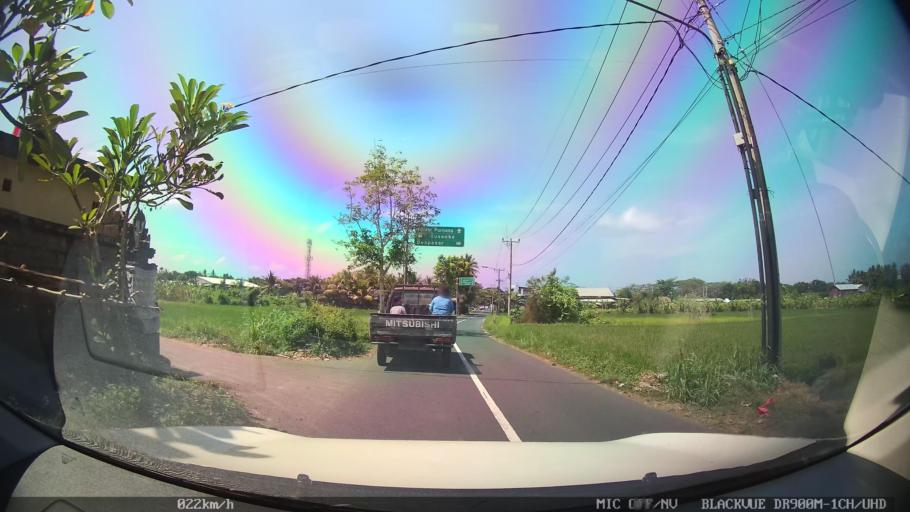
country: ID
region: Bali
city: Banjar Pasekan
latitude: -8.6113
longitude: 115.3064
